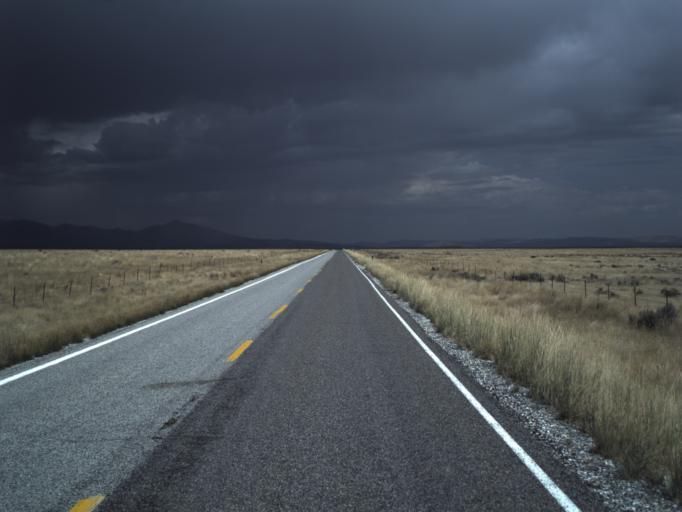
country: US
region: Idaho
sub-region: Oneida County
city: Malad City
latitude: 41.8753
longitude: -113.1205
